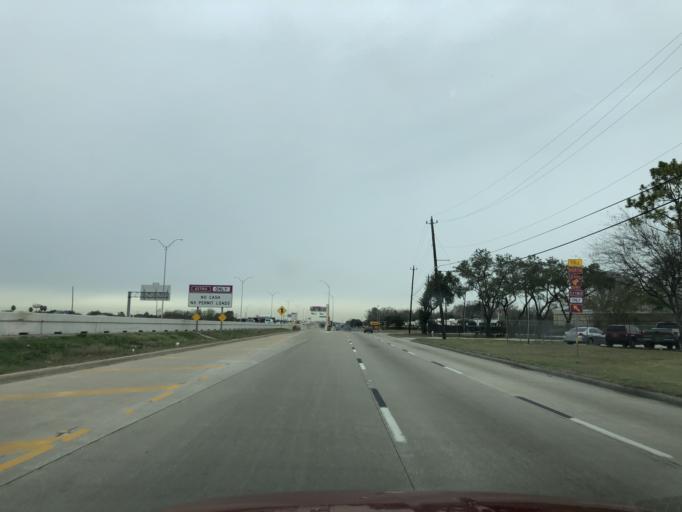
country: US
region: Texas
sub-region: Fort Bend County
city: Missouri City
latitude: 29.6319
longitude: -95.5241
